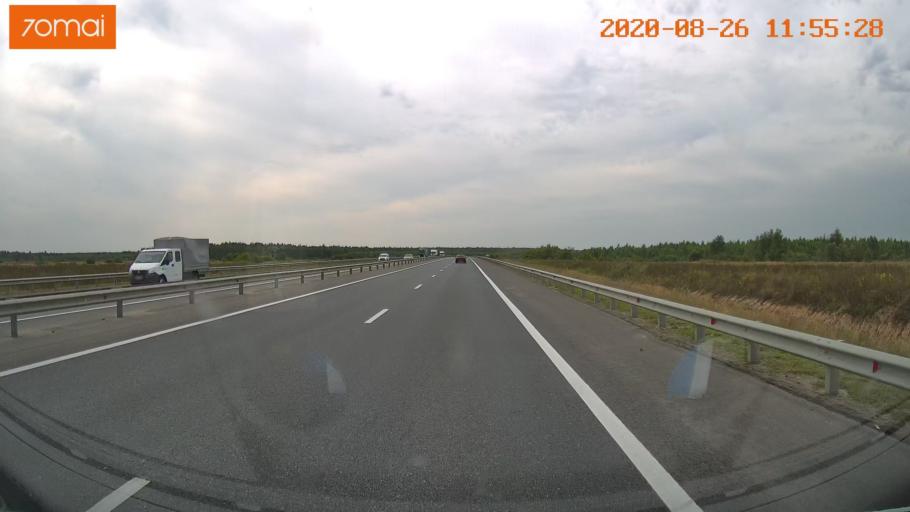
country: RU
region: Rjazan
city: Kiritsy
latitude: 54.2726
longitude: 40.3953
